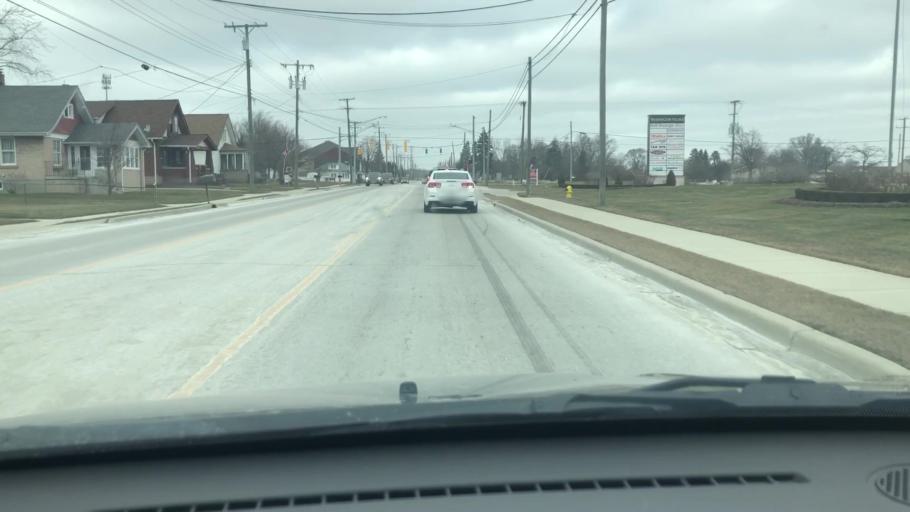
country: US
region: Michigan
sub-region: Macomb County
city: Shelby
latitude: 42.7269
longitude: -83.0358
